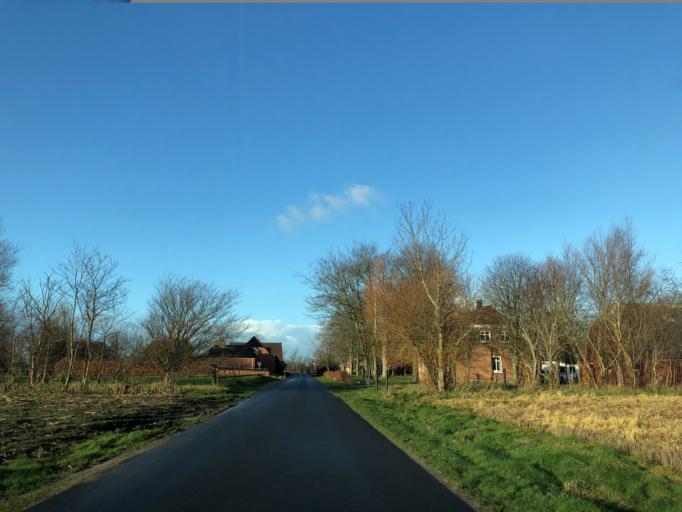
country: DK
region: Central Jutland
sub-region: Holstebro Kommune
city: Ulfborg
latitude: 56.2099
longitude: 8.2609
